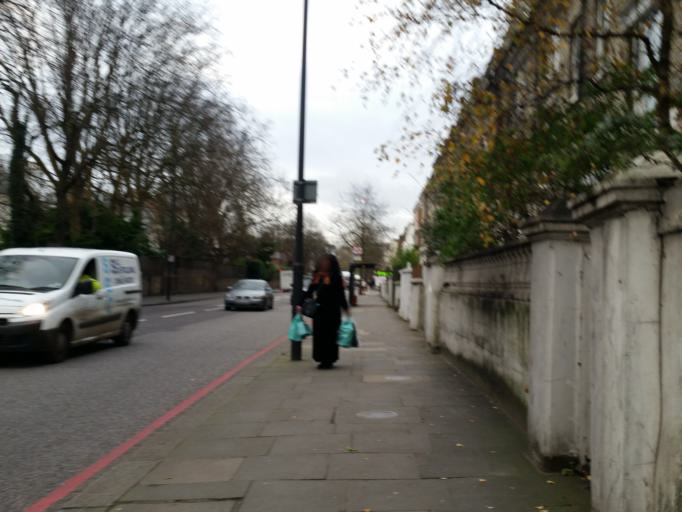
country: GB
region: England
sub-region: Greater London
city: Hammersmith
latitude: 51.5011
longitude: -0.2119
